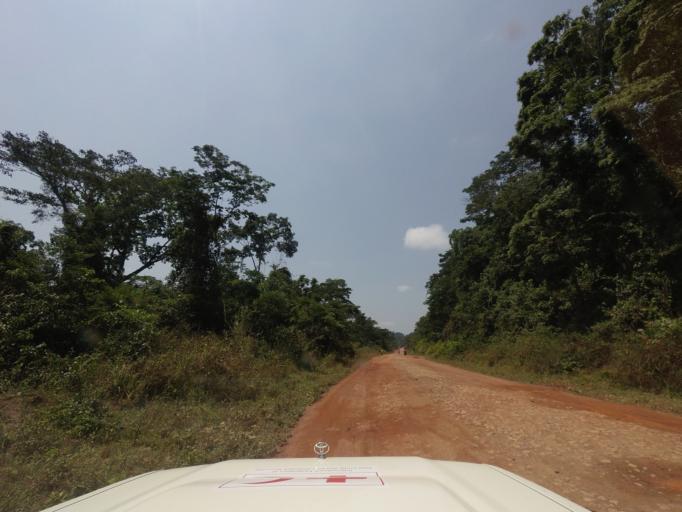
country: LR
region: Lofa
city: Voinjama
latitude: 8.3832
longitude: -9.7597
